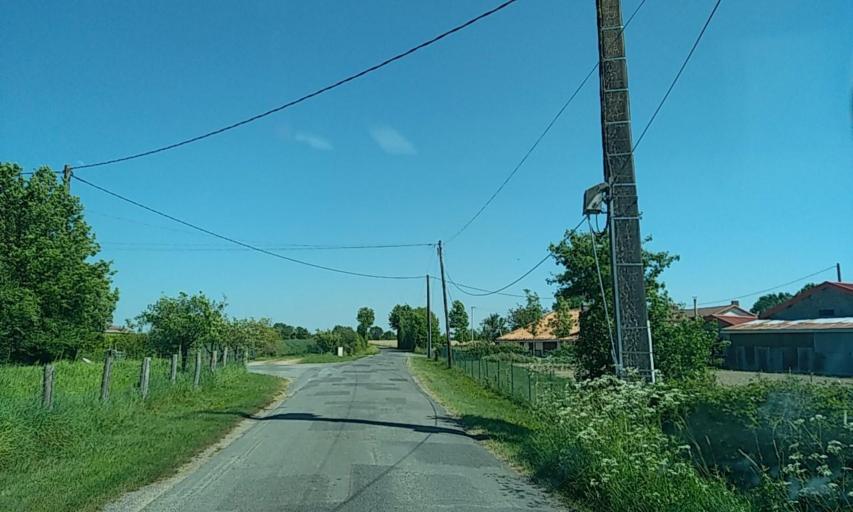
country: FR
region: Poitou-Charentes
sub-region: Departement des Deux-Sevres
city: La Chapelle-Saint-Laurent
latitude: 46.7697
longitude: -0.4666
